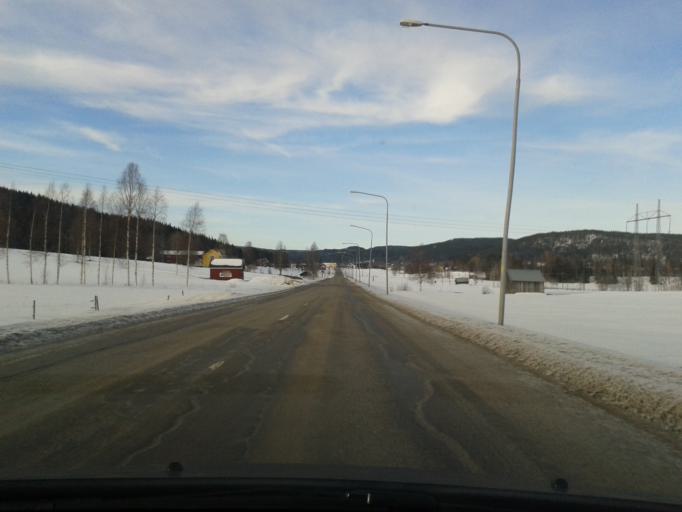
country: SE
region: Vaesternorrland
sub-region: OErnskoeldsviks Kommun
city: Bredbyn
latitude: 63.5041
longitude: 18.0744
